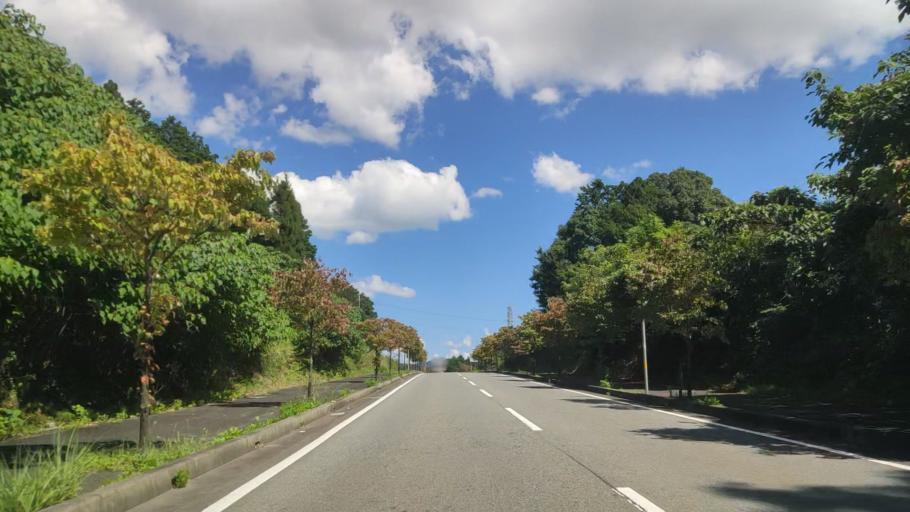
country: JP
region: Kyoto
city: Fukuchiyama
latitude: 35.2495
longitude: 135.1353
